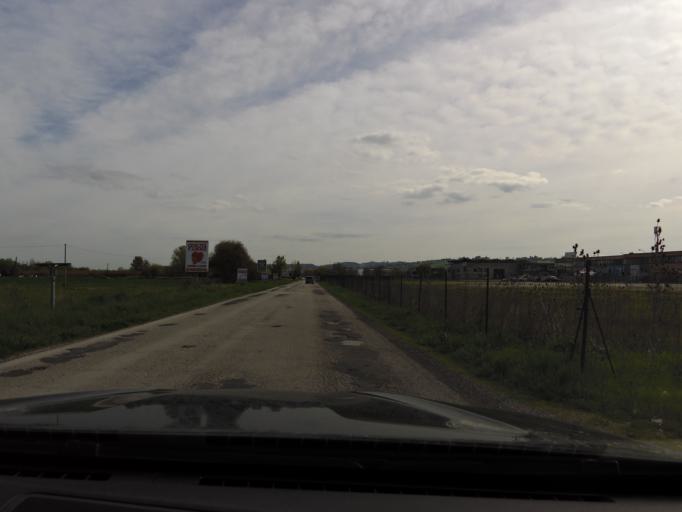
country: IT
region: The Marches
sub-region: Provincia di Ancona
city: Camerano
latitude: 43.5189
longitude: 13.5291
